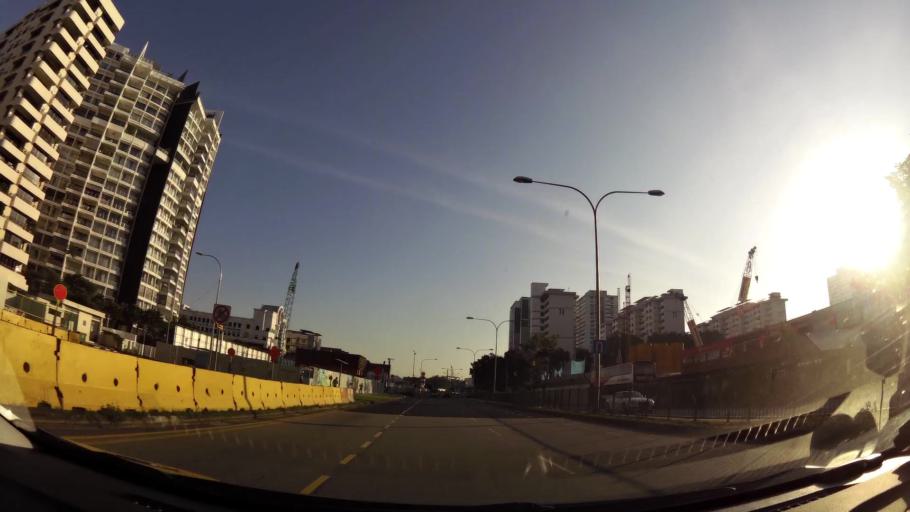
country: SG
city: Singapore
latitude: 1.3031
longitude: 103.9057
